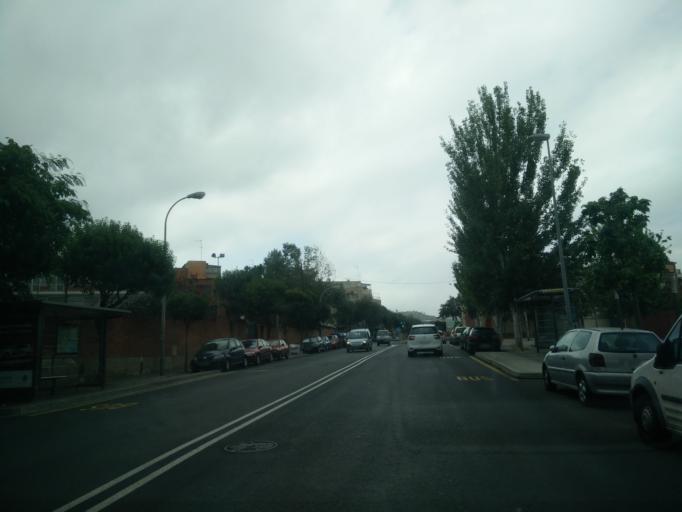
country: ES
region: Catalonia
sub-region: Provincia de Barcelona
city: Llefia
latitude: 41.4485
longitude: 2.2244
